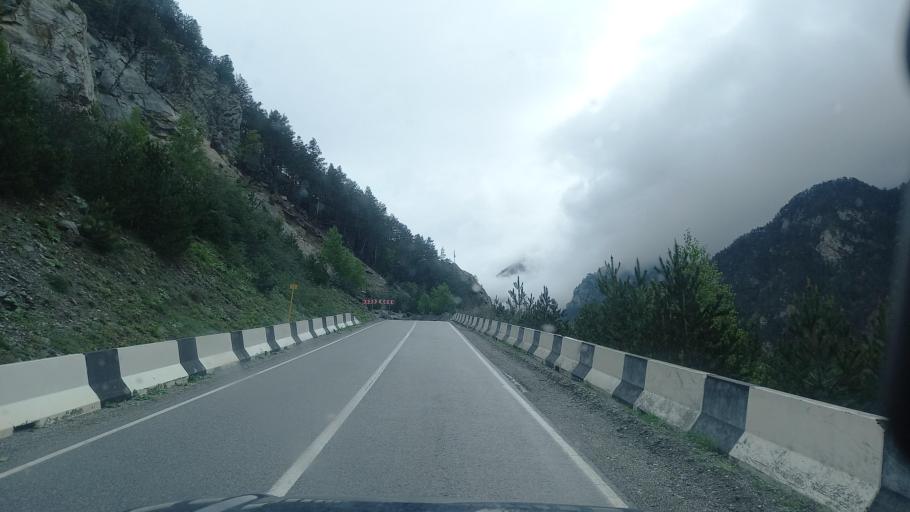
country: RU
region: North Ossetia
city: Mizur
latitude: 42.7941
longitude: 44.0015
